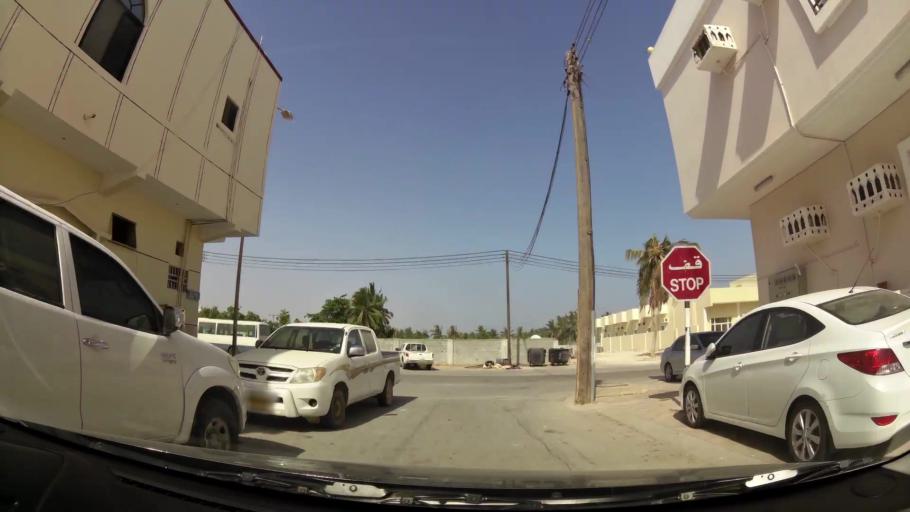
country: OM
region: Zufar
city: Salalah
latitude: 17.0037
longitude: 54.0523
